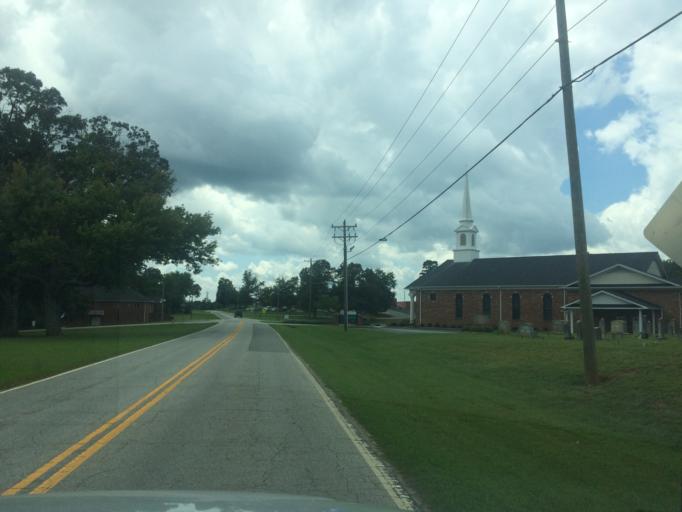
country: US
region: South Carolina
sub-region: Spartanburg County
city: Inman
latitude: 35.1313
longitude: -82.0446
